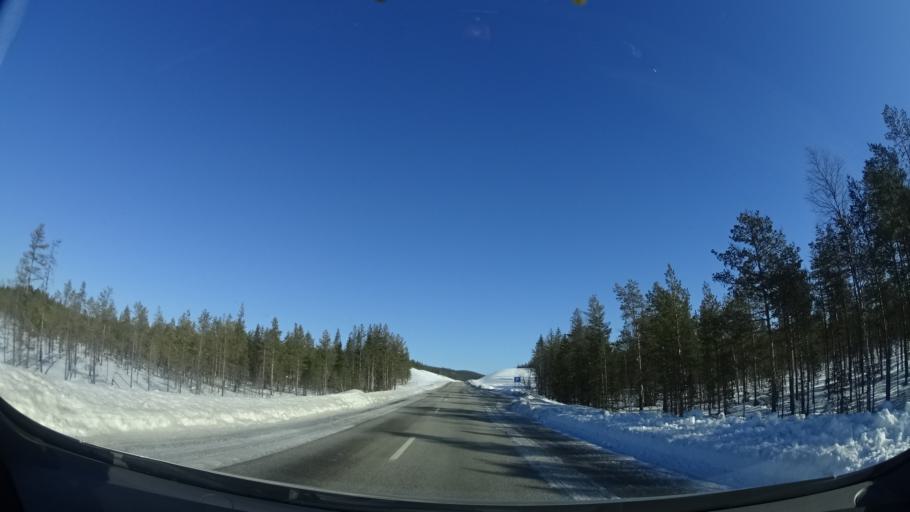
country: SE
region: Vaesterbotten
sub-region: Skelleftea Kommun
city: Langsele
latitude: 65.1127
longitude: 20.0847
